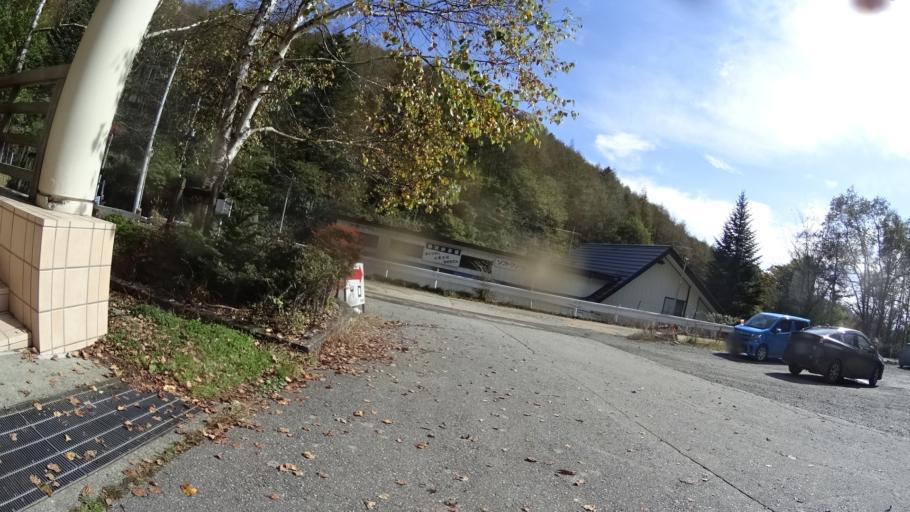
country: JP
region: Yamanashi
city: Enzan
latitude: 35.7757
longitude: 138.8021
